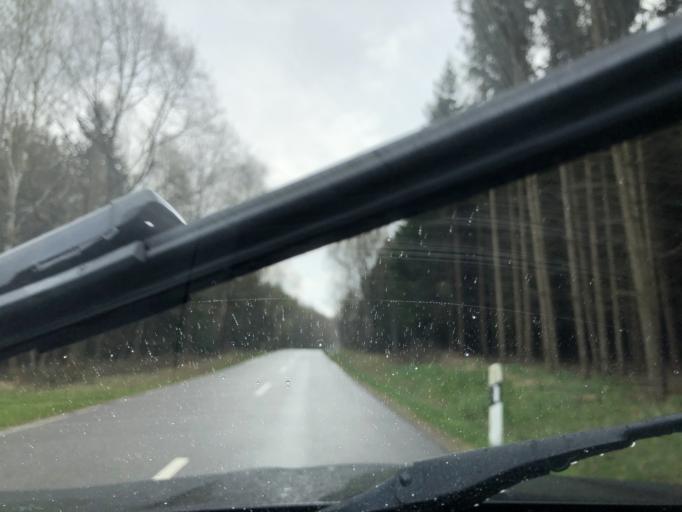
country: DE
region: Bavaria
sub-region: Upper Bavaria
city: Wolfersdorf
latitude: 48.4954
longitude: 11.6906
